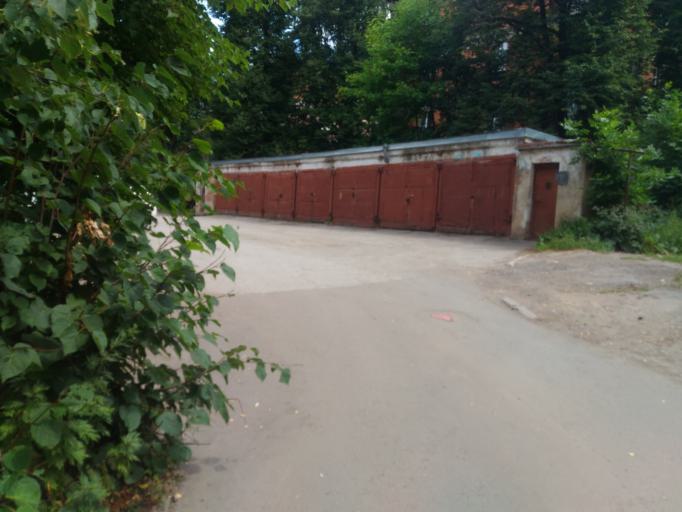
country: RU
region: Tula
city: Mendeleyevskiy
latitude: 54.1696
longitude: 37.5763
